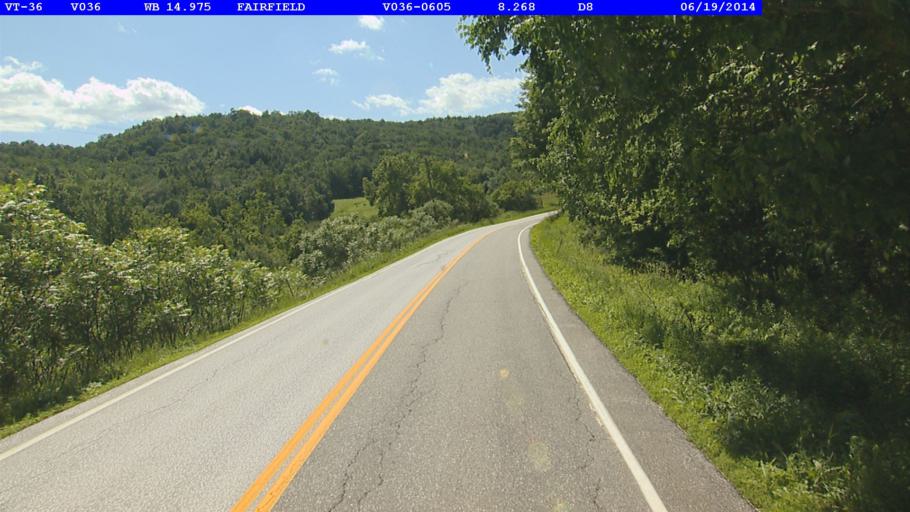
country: US
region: Vermont
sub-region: Franklin County
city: Enosburg Falls
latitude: 44.7939
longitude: -72.8775
